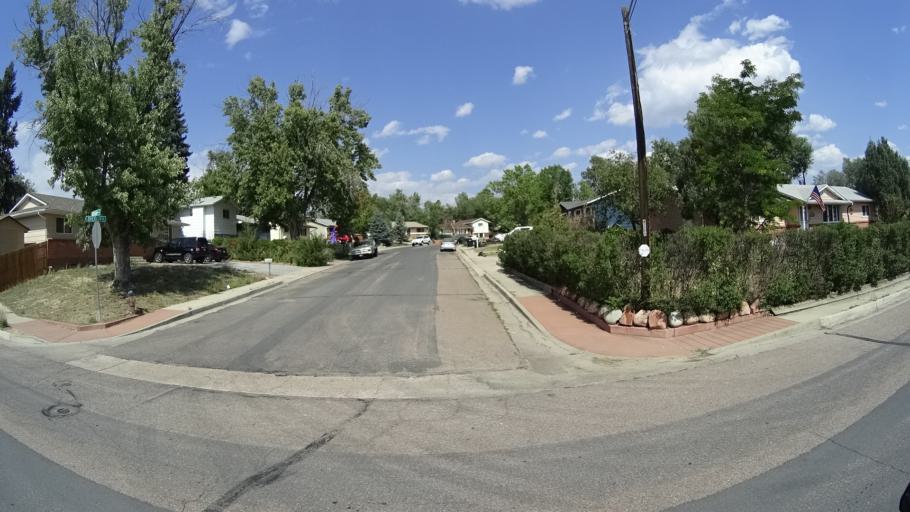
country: US
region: Colorado
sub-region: El Paso County
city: Stratmoor
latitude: 38.8260
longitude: -104.7651
